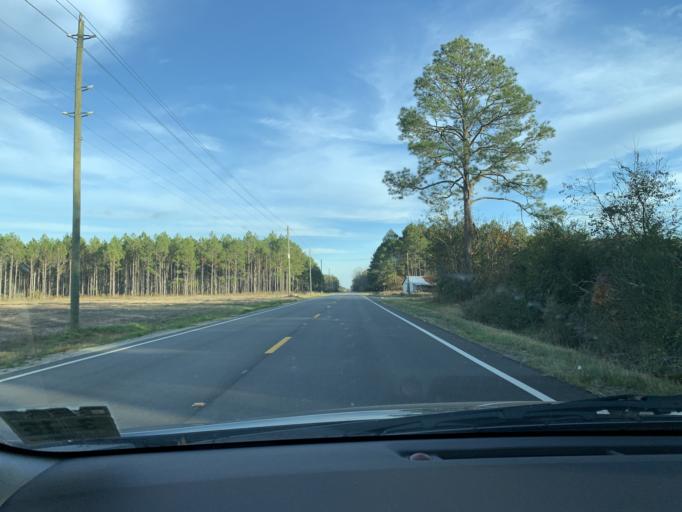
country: US
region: Georgia
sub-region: Irwin County
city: Ocilla
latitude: 31.5845
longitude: -83.0746
